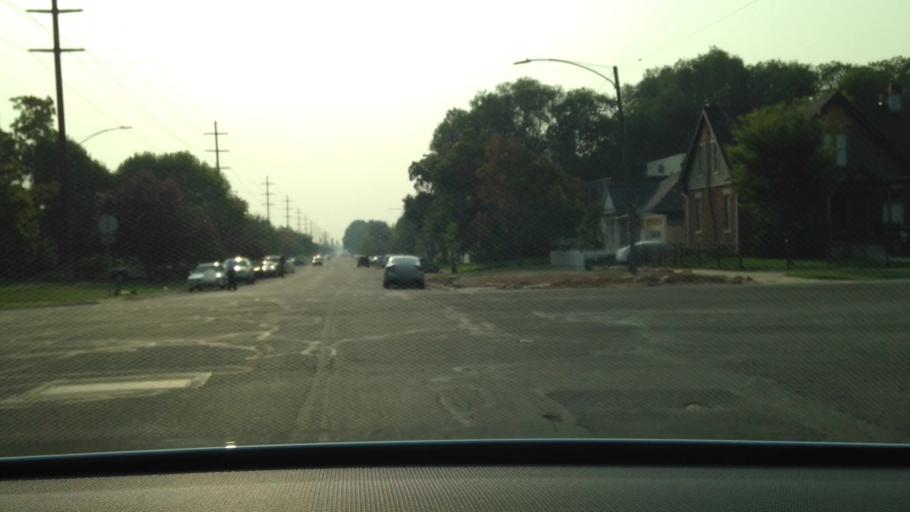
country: US
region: Utah
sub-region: Salt Lake County
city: Salt Lake City
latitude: 40.7542
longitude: -111.8737
